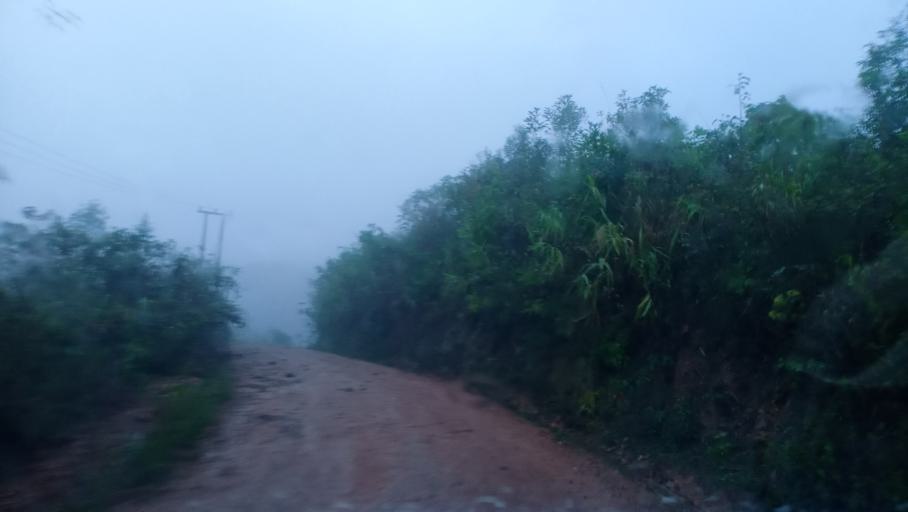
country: LA
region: Phongsali
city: Khoa
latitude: 21.2104
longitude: 102.2592
